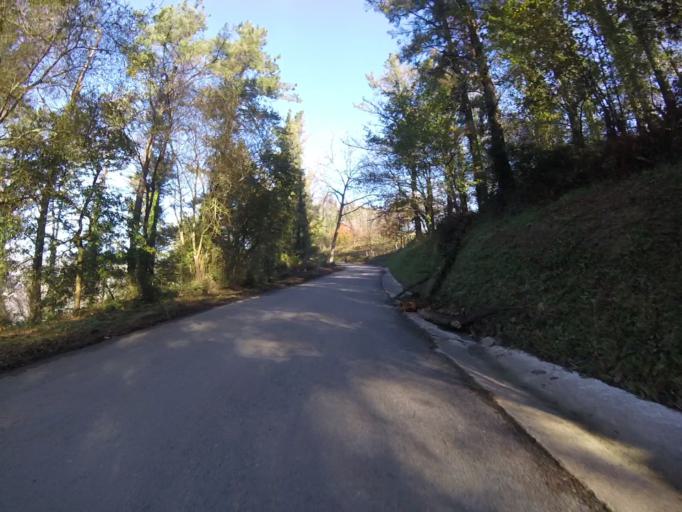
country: ES
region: Basque Country
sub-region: Provincia de Guipuzcoa
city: Usurbil
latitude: 43.2787
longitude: -2.0701
